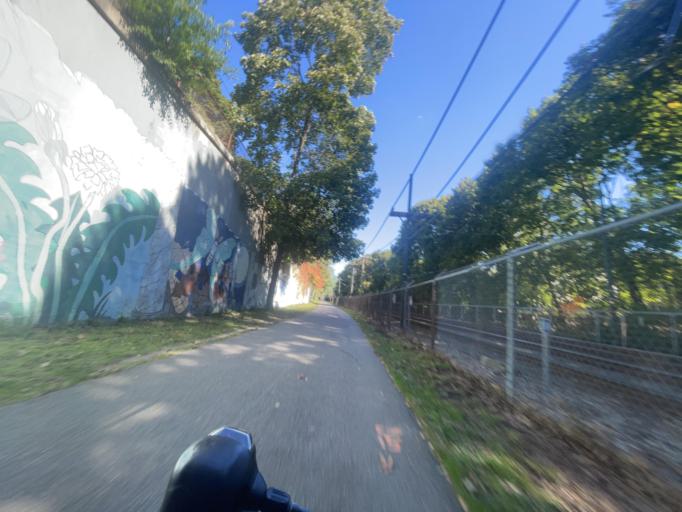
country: US
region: Massachusetts
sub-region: Norfolk County
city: Milton
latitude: 42.2712
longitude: -71.0646
